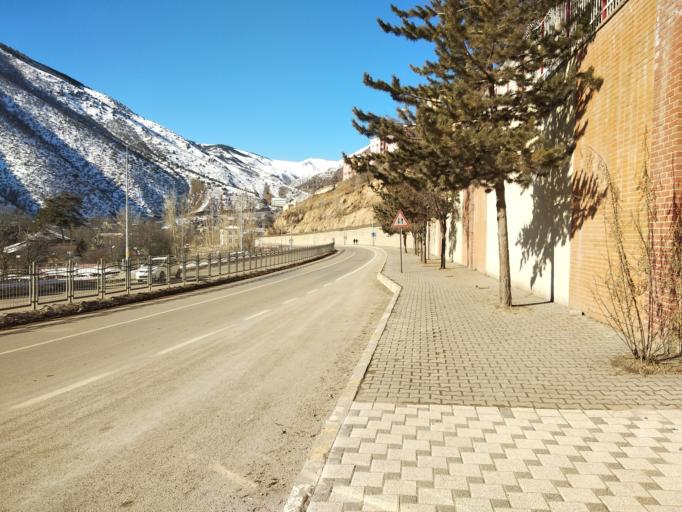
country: TR
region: Gumushane
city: Gumushkhane
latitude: 40.4366
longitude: 39.5130
